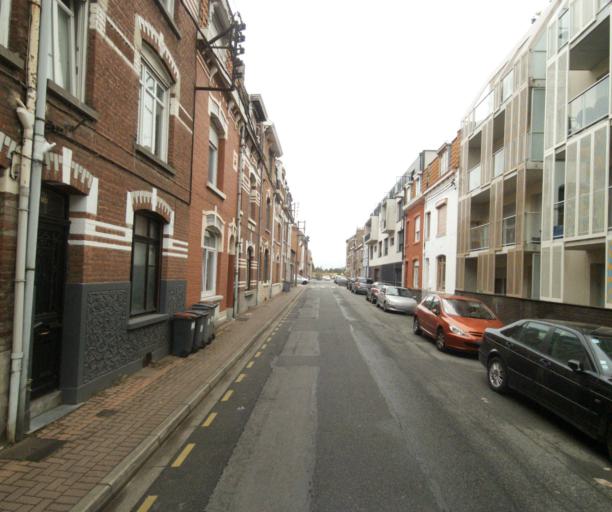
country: FR
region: Nord-Pas-de-Calais
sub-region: Departement du Nord
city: Lille
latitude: 50.6127
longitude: 3.0704
